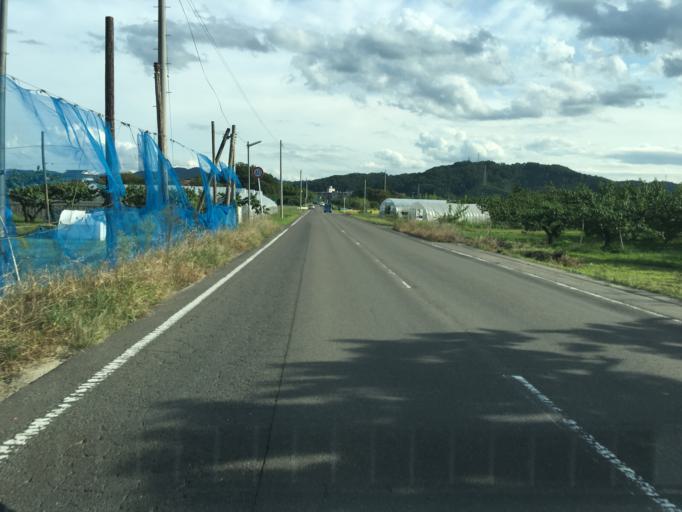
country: JP
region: Fukushima
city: Hobaramachi
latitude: 37.8192
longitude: 140.5384
